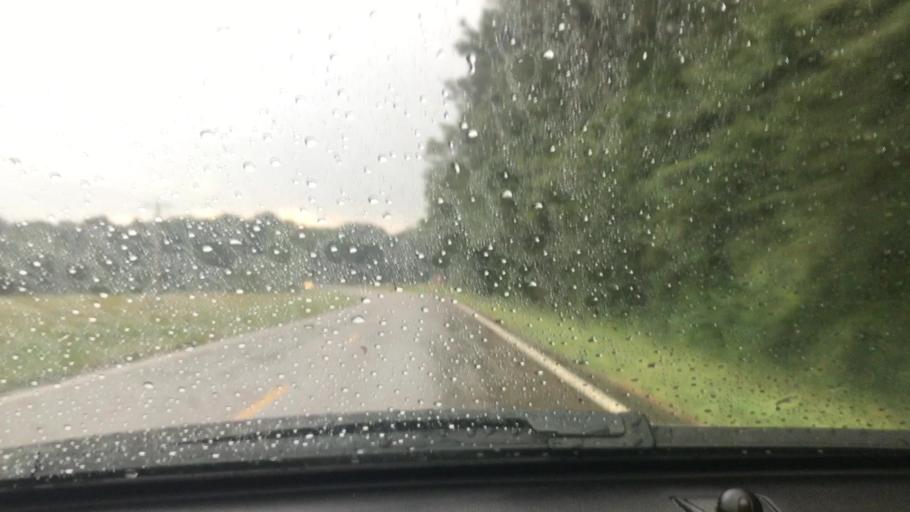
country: US
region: Mississippi
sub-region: Pike County
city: Summit
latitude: 31.3236
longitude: -90.5437
